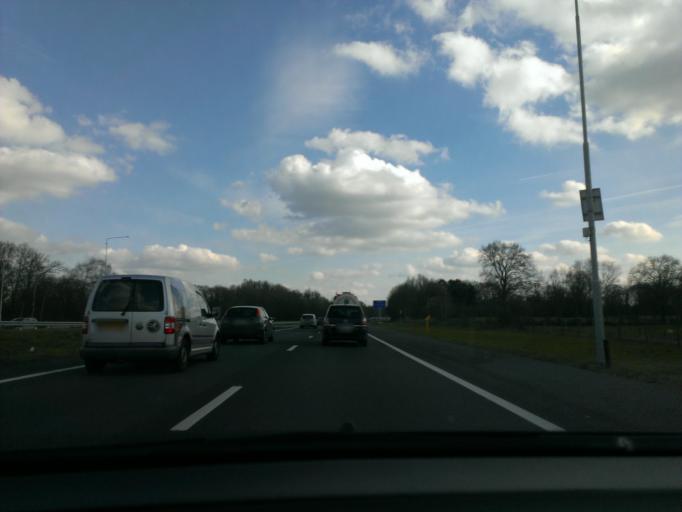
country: NL
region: Overijssel
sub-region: Gemeente Borne
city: Borne
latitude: 52.2829
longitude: 6.7437
